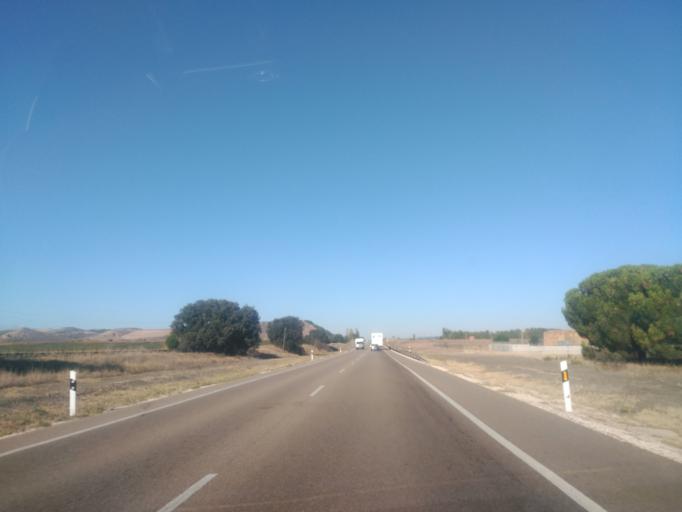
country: ES
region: Castille and Leon
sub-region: Provincia de Valladolid
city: Manzanillo
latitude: 41.6140
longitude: -4.1833
